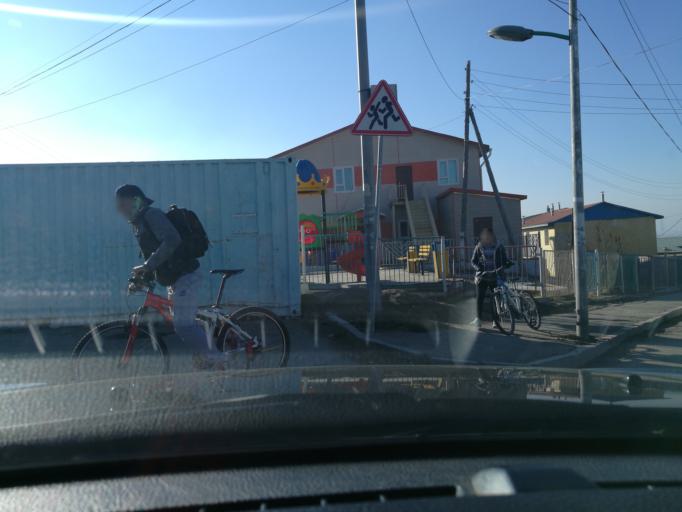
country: MN
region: Ulaanbaatar
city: Ulaanbaatar
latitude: 47.9696
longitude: 106.9307
